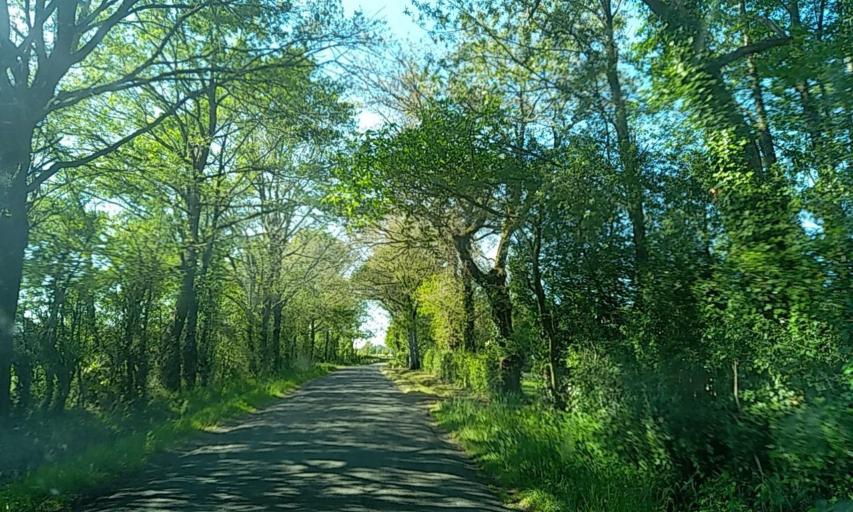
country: FR
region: Poitou-Charentes
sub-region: Departement des Deux-Sevres
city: Boisme
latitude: 46.8079
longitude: -0.4502
